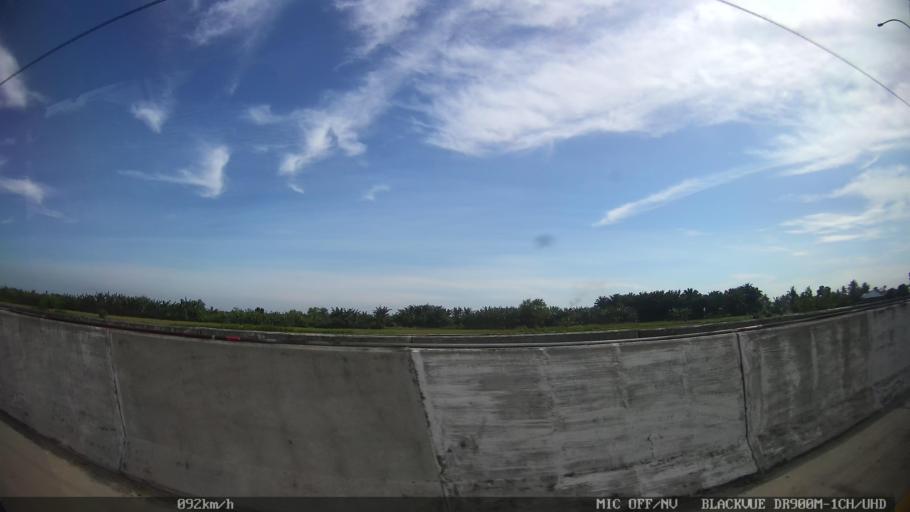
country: ID
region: North Sumatra
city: Sunggal
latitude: 3.6415
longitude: 98.5673
